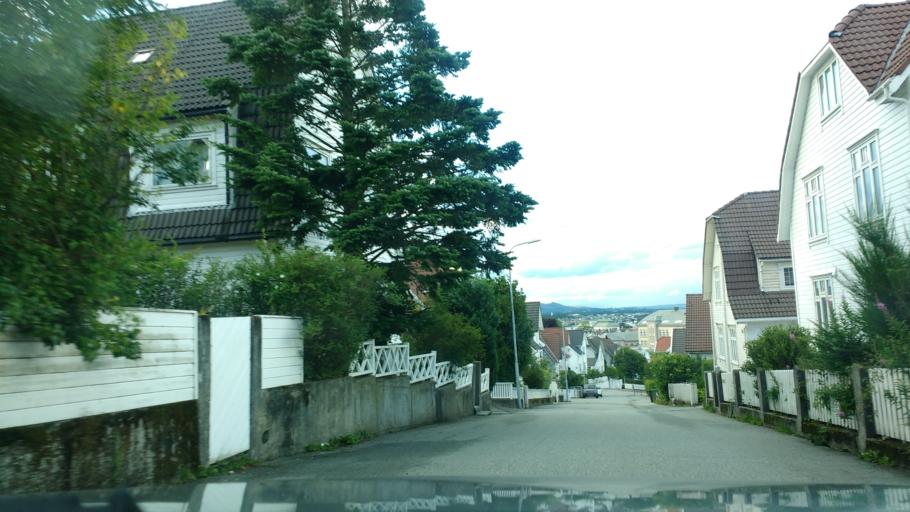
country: NO
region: Rogaland
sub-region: Stavanger
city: Stavanger
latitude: 58.9593
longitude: 5.7315
